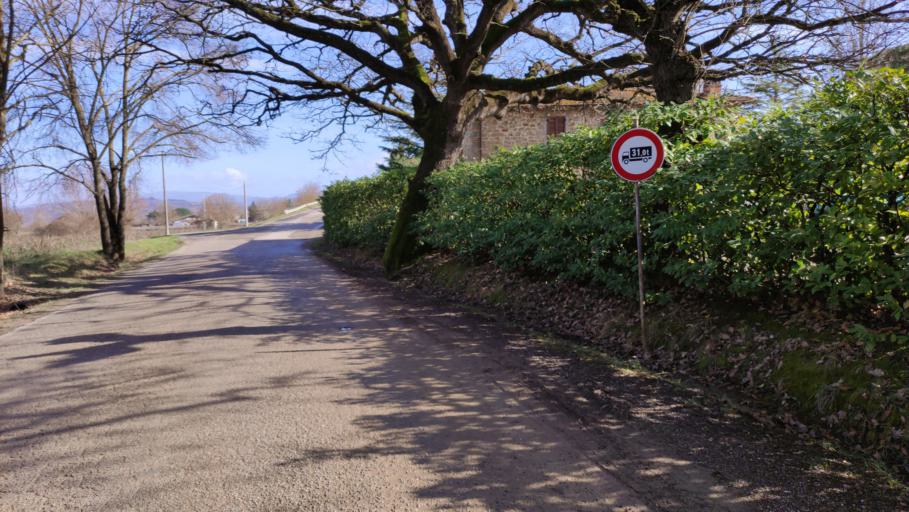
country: IT
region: Tuscany
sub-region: Province of Arezzo
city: Viciomaggio
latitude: 43.4223
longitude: 11.7828
